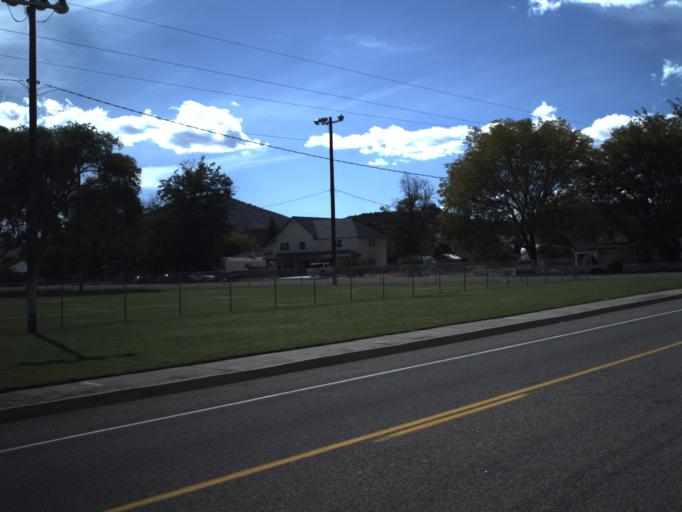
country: US
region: Utah
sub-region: Washington County
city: Enterprise
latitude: 37.5736
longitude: -113.7227
